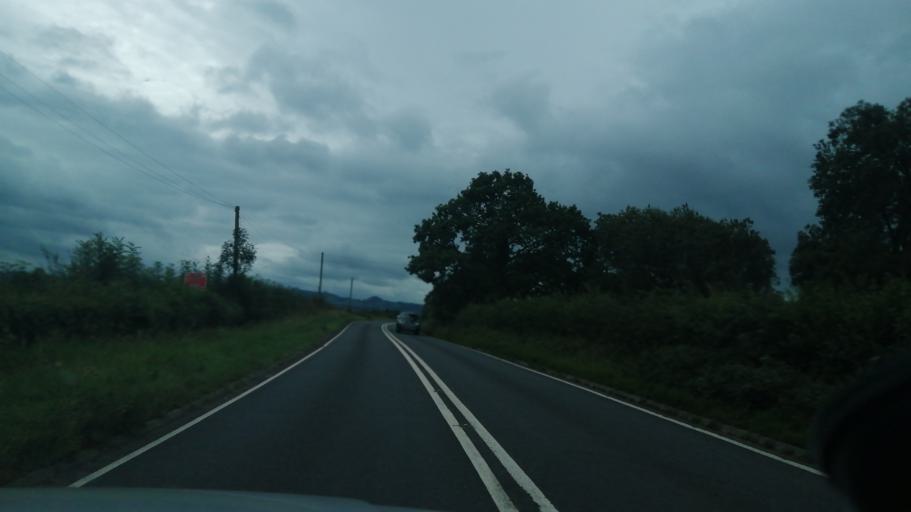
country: GB
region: England
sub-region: Herefordshire
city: Thruxton
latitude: 52.0071
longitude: -2.7914
